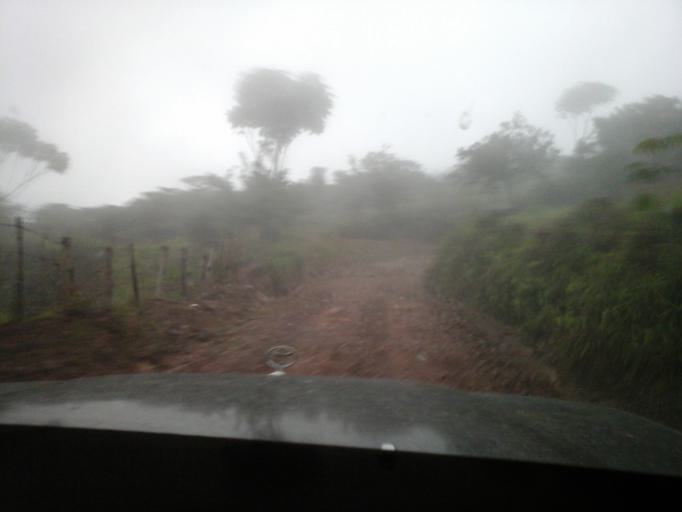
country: CO
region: Cesar
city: Agustin Codazzi
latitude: 9.9400
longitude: -73.1470
